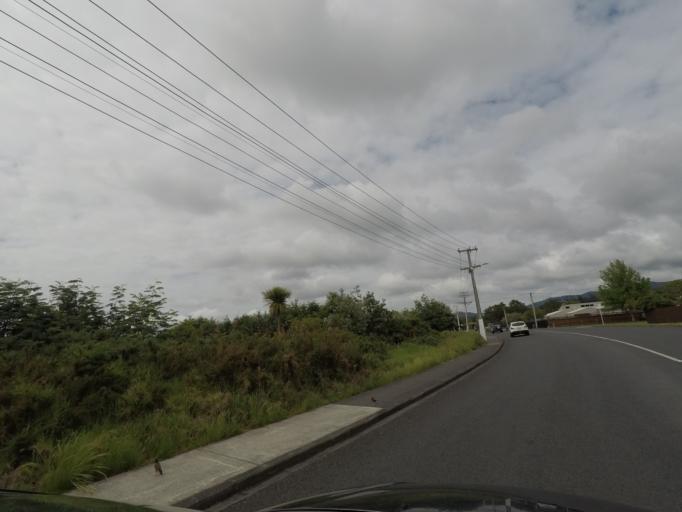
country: NZ
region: Auckland
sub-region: Auckland
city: Waitakere
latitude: -36.9002
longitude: 174.6227
